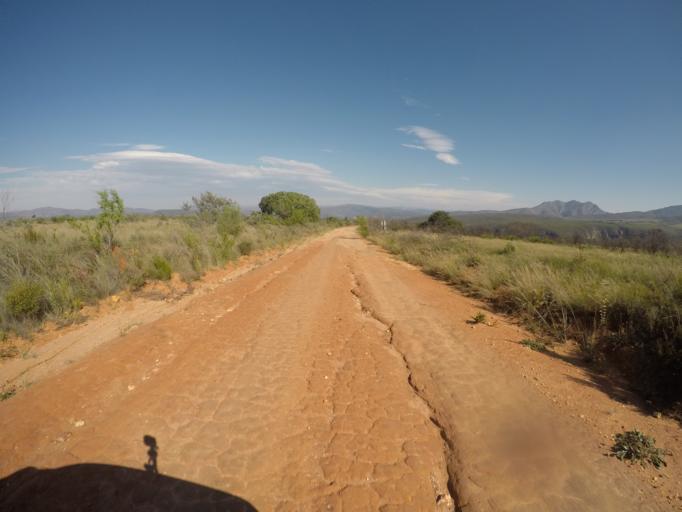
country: ZA
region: Eastern Cape
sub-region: Cacadu District Municipality
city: Kareedouw
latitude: -33.6359
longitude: 24.4609
